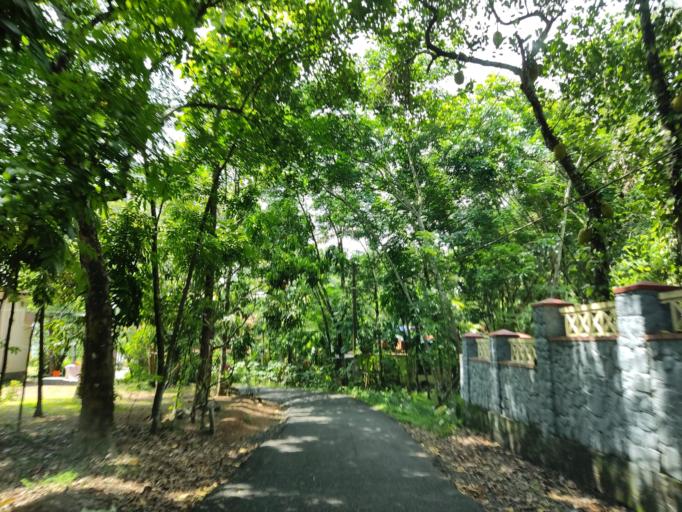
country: IN
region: Kerala
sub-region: Alappuzha
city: Chengannur
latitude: 9.3033
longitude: 76.5837
